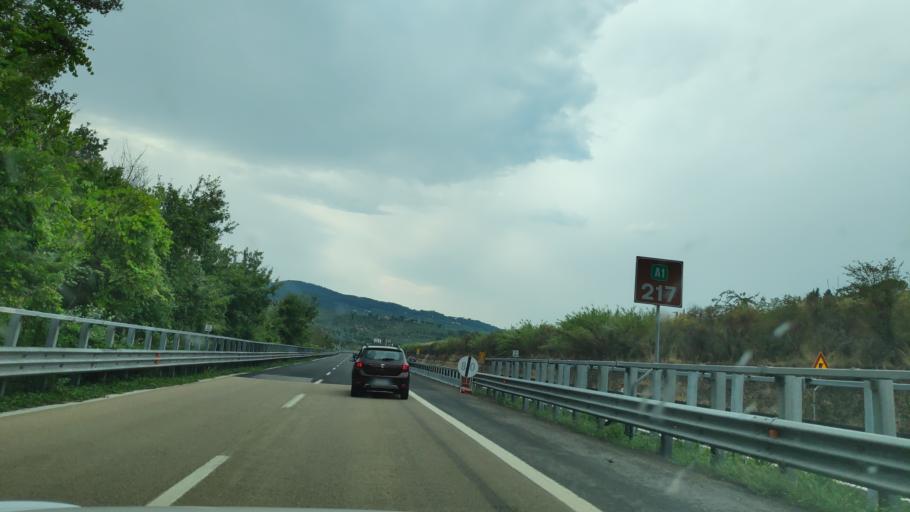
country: IT
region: Tuscany
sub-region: Province of Florence
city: Scandicci
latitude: 43.7310
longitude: 11.1970
